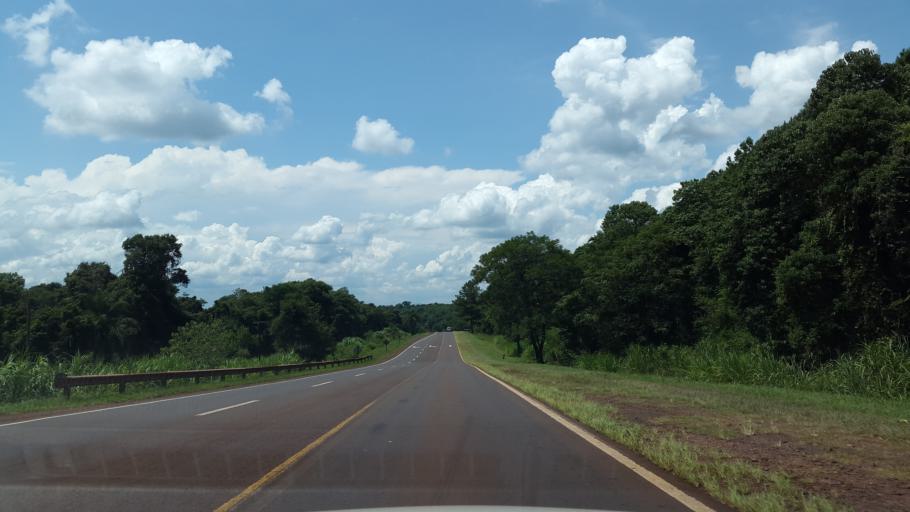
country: AR
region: Misiones
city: El Alcazar
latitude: -26.7226
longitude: -54.8632
